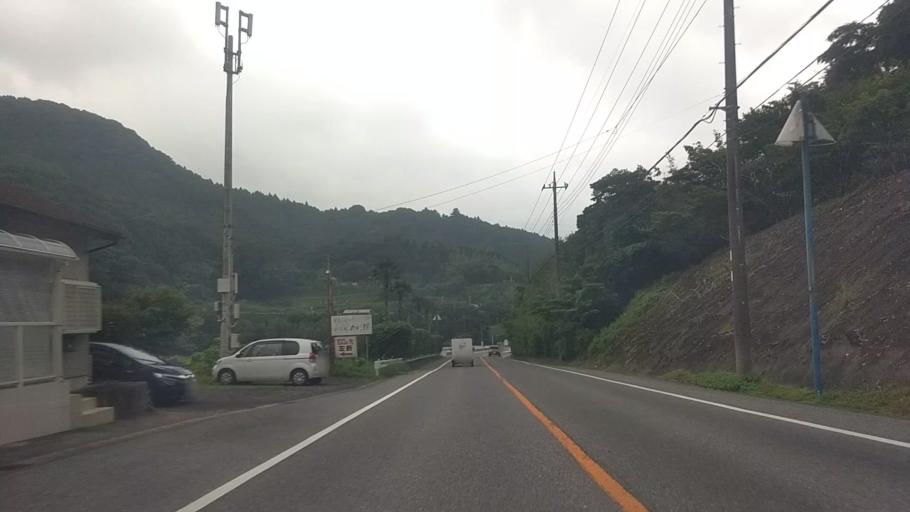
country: JP
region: Chiba
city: Kawaguchi
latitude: 35.1450
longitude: 140.0688
